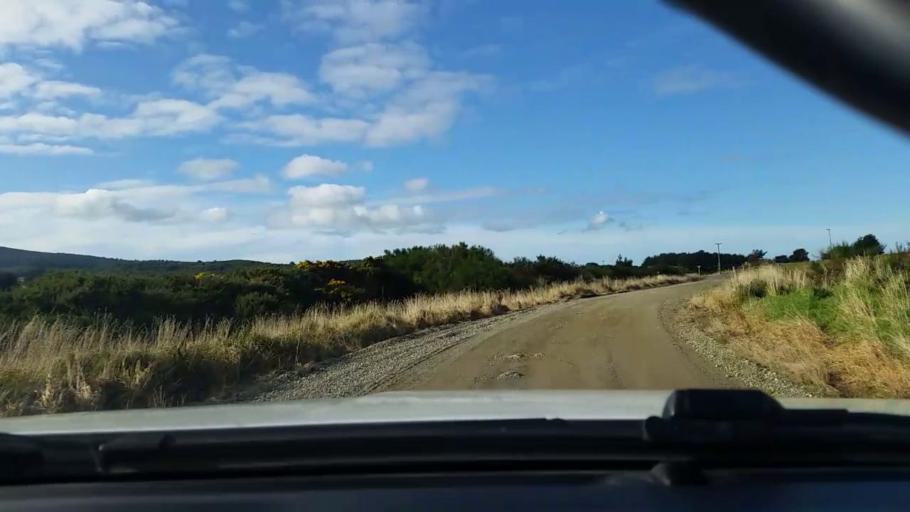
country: NZ
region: Southland
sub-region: Southland District
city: Riverton
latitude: -46.3328
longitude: 167.8193
